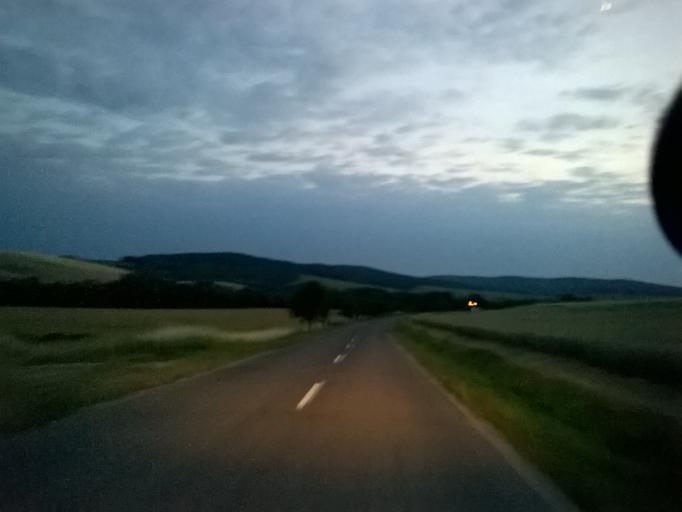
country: SK
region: Trnavsky
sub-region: Okres Senica
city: Senica
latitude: 48.7476
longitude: 17.3181
